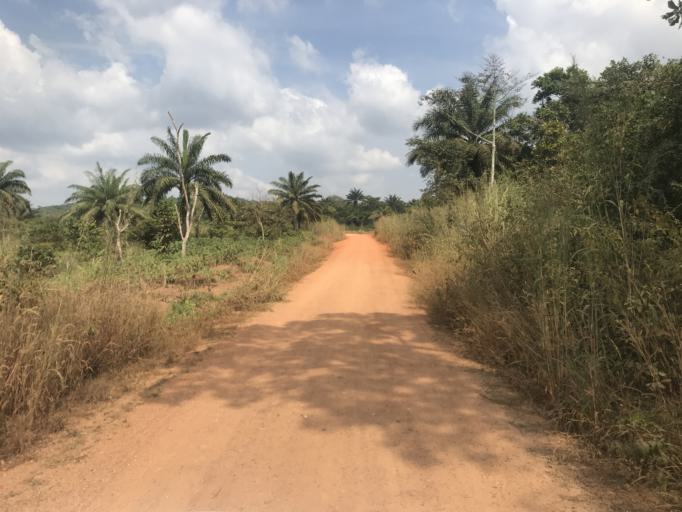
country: NG
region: Osun
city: Inisa
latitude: 7.8905
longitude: 4.3963
